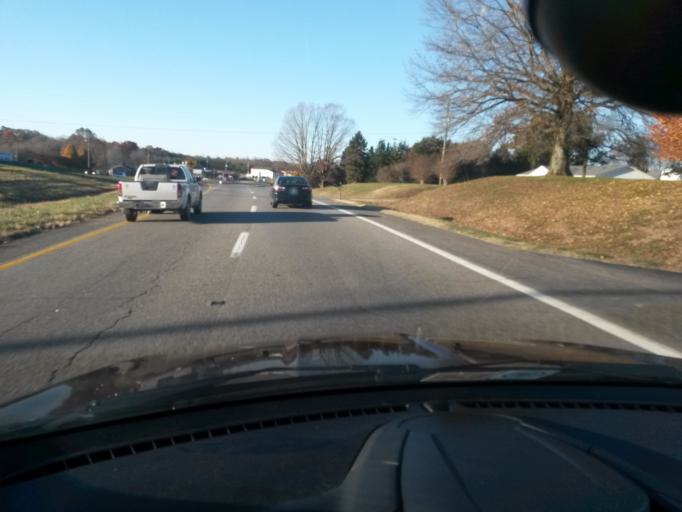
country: US
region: Virginia
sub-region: Henry County
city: Horse Pasture
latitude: 36.6266
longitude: -79.9552
